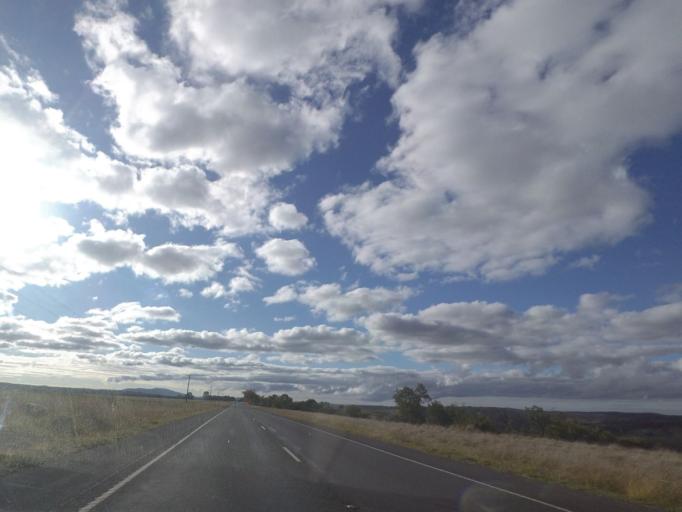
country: AU
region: Victoria
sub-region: Mount Alexander
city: Castlemaine
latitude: -37.1689
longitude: 144.3583
